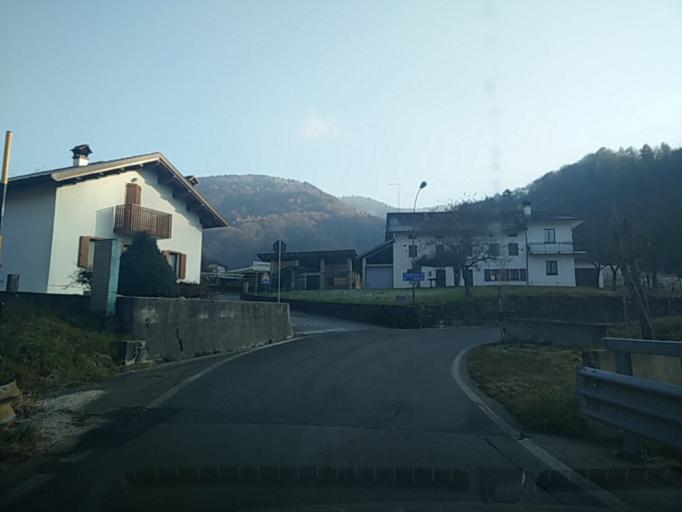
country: IT
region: Veneto
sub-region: Provincia di Belluno
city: Trichiana
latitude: 46.0369
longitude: 12.1674
